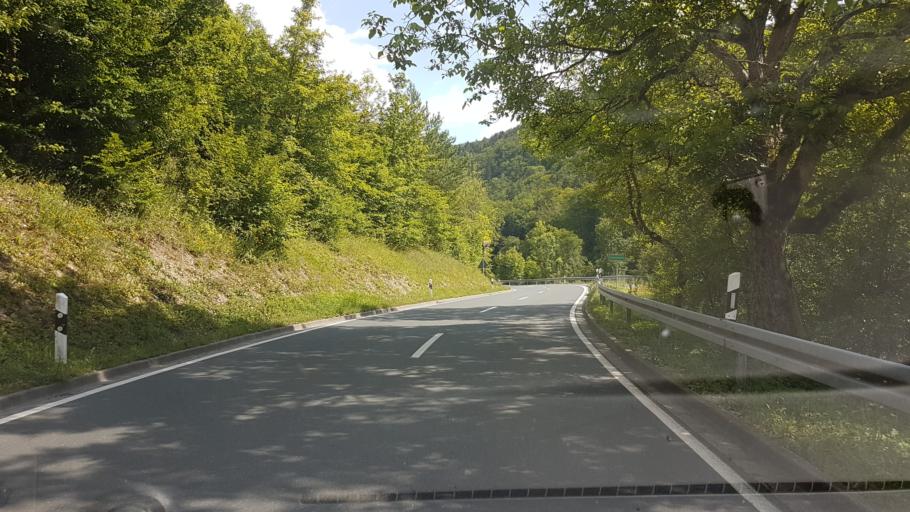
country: DE
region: Bavaria
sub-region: Upper Franconia
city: Egloffstein
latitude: 49.7469
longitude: 11.2391
